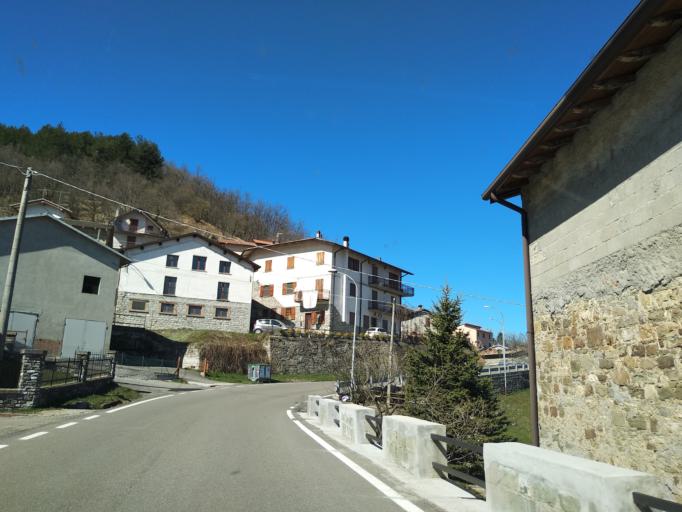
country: IT
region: Emilia-Romagna
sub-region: Provincia di Reggio Emilia
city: Ramiseto
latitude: 44.4139
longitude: 10.3006
